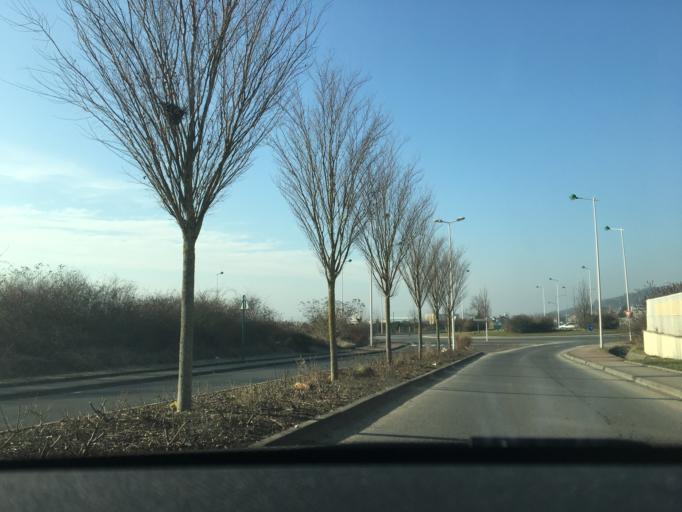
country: FR
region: Ile-de-France
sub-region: Departement des Yvelines
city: Limay
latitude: 48.9957
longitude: 1.7515
